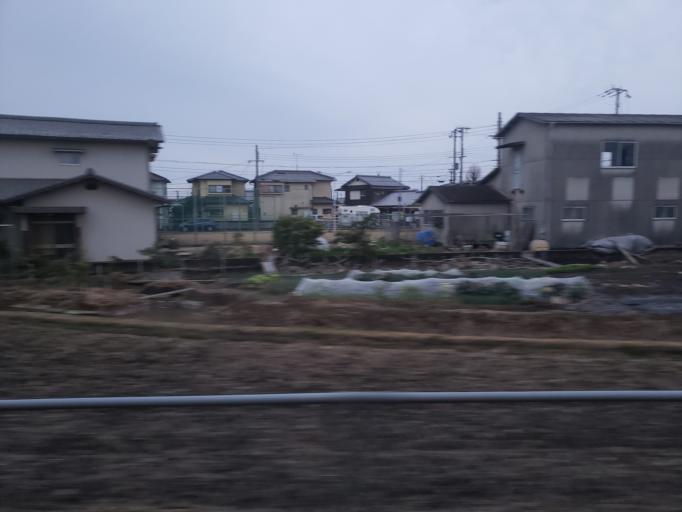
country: JP
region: Hyogo
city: Kakogawacho-honmachi
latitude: 34.7352
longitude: 134.8786
